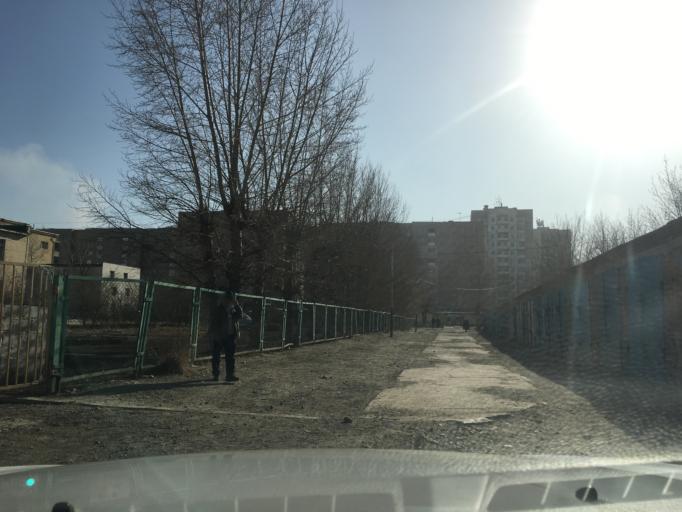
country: MN
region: Ulaanbaatar
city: Ulaanbaatar
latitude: 47.9151
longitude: 106.8429
